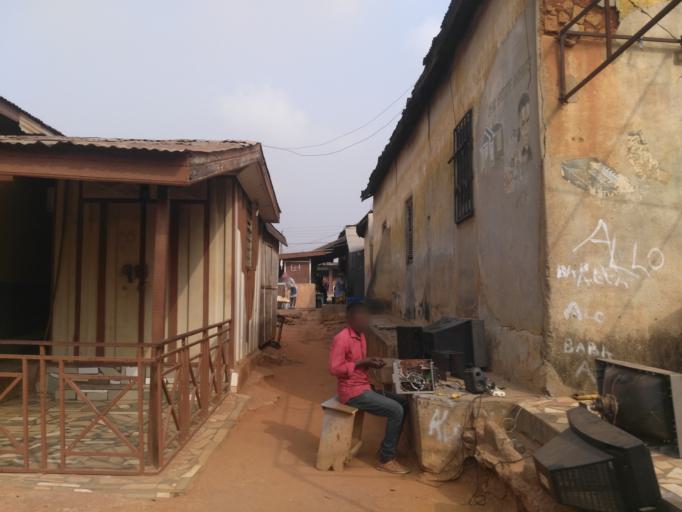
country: GH
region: Ashanti
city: Kumasi
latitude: 6.6923
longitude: -1.6170
